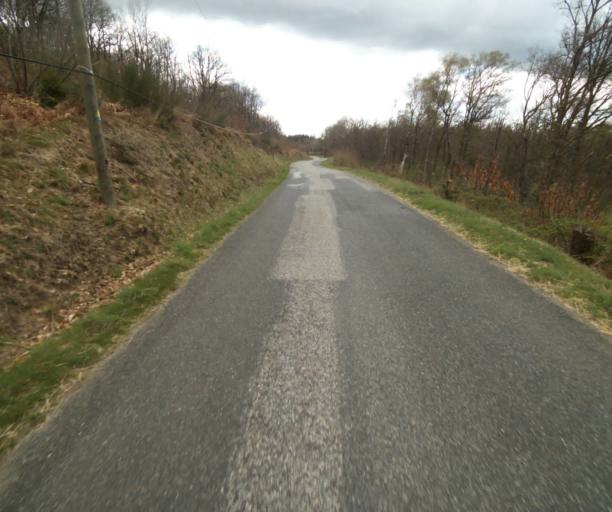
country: FR
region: Limousin
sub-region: Departement de la Correze
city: Correze
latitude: 45.2662
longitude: 1.9003
